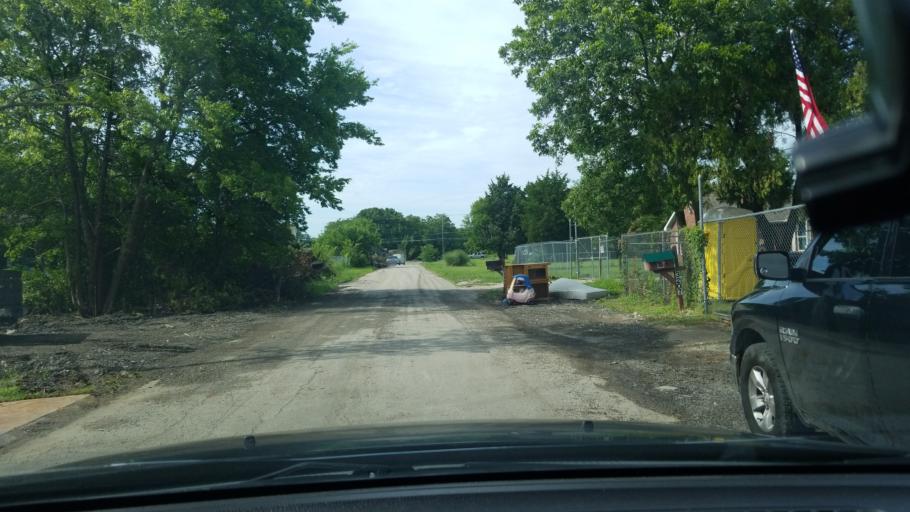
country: US
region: Texas
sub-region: Dallas County
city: Balch Springs
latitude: 32.7649
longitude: -96.6647
